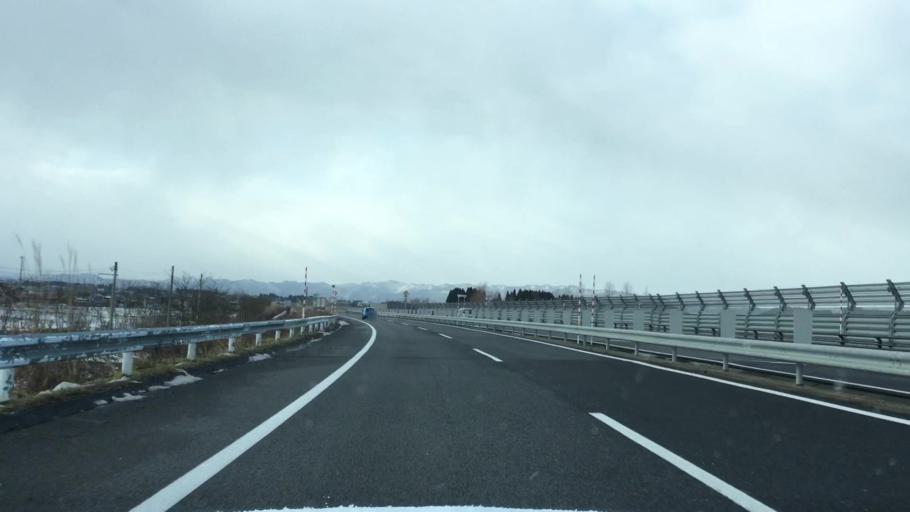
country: JP
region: Akita
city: Odate
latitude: 40.2994
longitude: 140.5557
